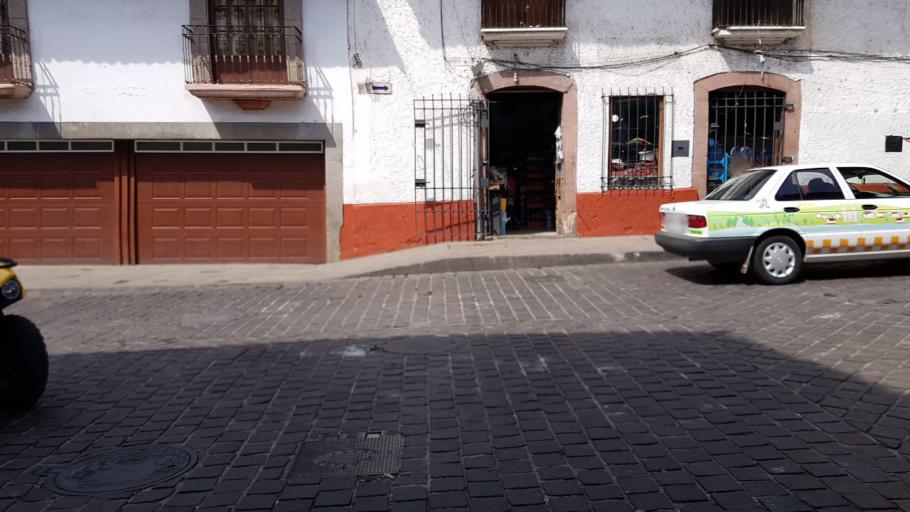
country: MX
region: Mexico
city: Valle de Bravo
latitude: 19.1940
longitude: -100.1308
